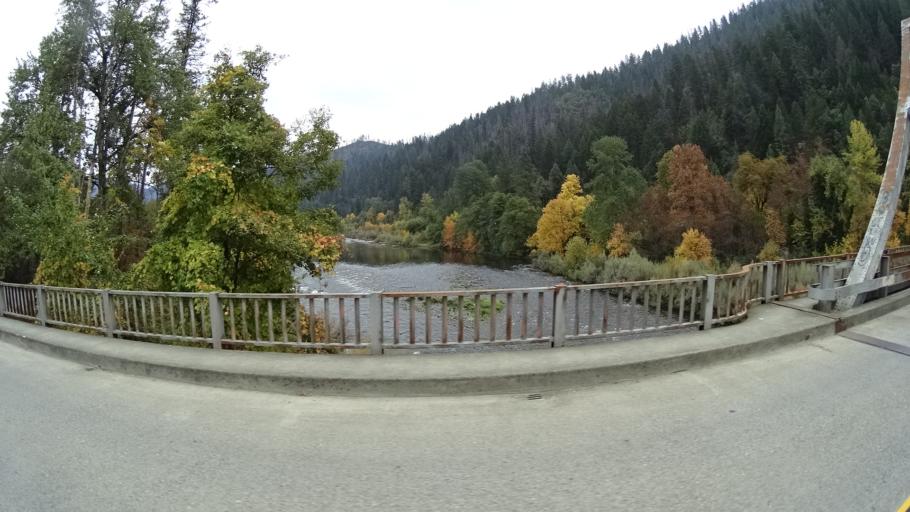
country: US
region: California
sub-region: Siskiyou County
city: Happy Camp
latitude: 41.7906
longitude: -123.3776
